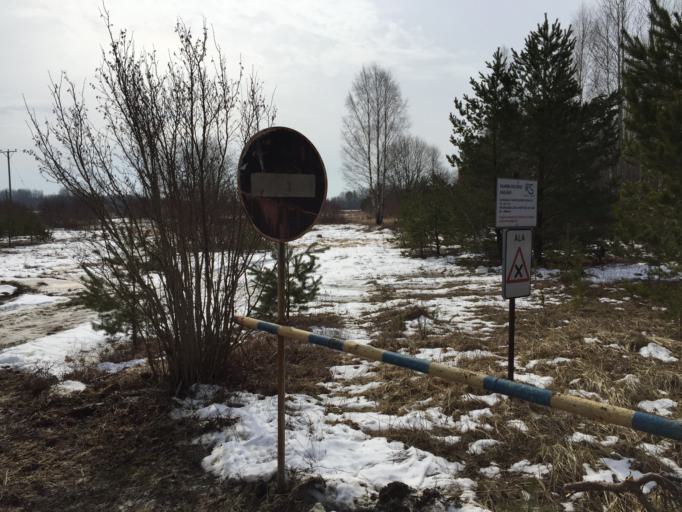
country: EE
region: Saare
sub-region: Kuressaare linn
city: Kuressaare
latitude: 58.3389
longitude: 22.4710
